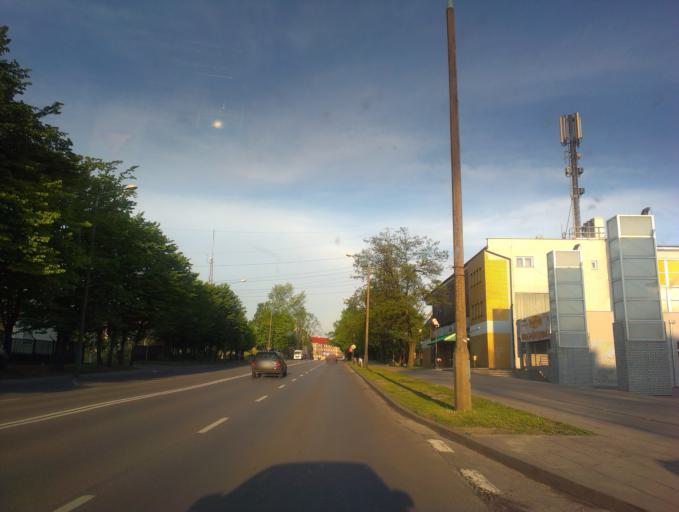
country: PL
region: Masovian Voivodeship
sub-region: Radom
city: Radom
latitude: 51.3975
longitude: 21.1471
